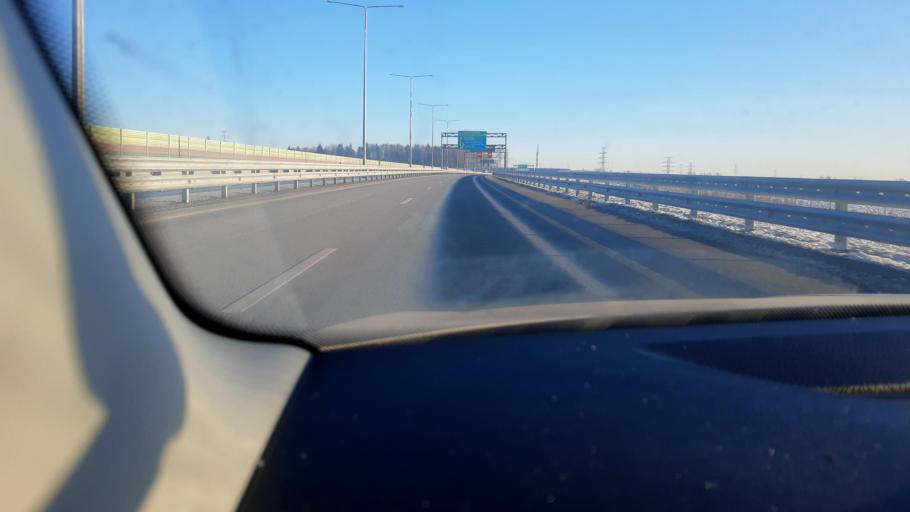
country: RU
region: Moskovskaya
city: Peshki
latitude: 56.1437
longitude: 37.0245
